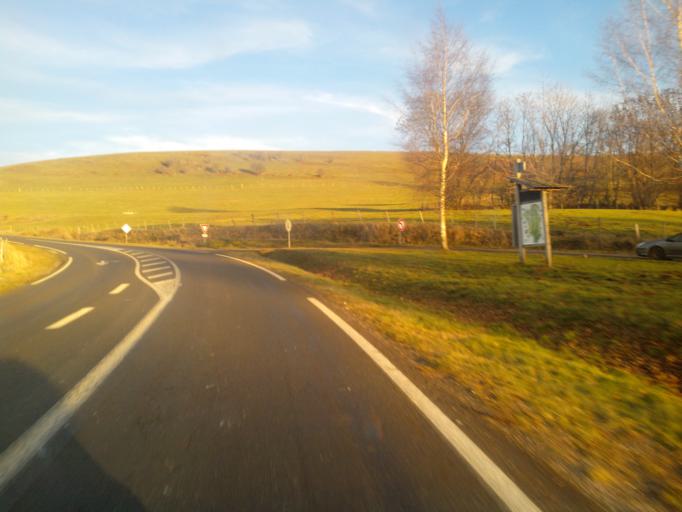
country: FR
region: Auvergne
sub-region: Departement du Cantal
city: Riom-es-Montagnes
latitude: 45.2347
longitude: 2.7341
